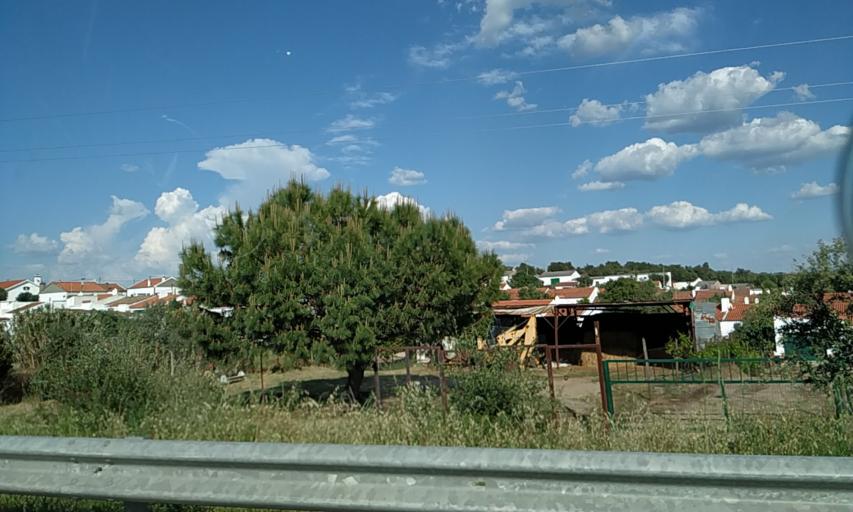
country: PT
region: Evora
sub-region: Estremoz
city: Estremoz
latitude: 38.9593
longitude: -7.5101
